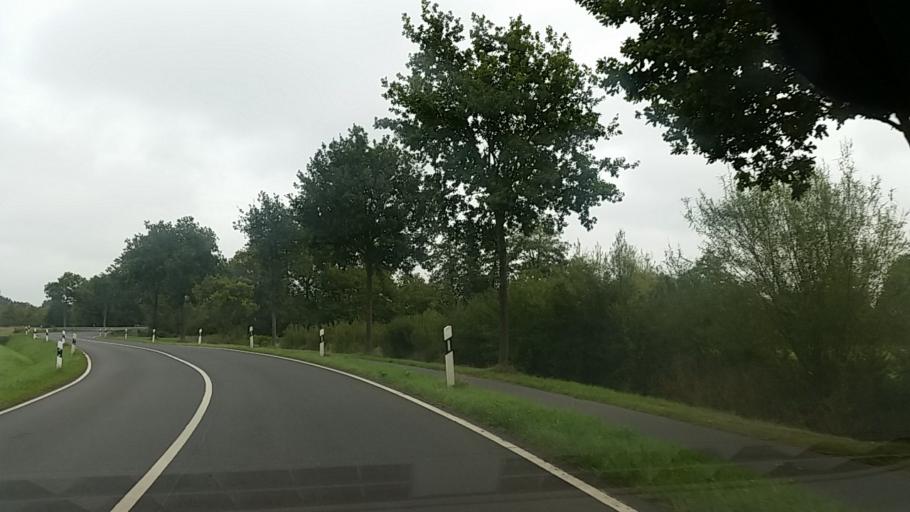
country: DE
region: Schleswig-Holstein
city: Kaltenkirchen
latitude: 53.8497
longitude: 9.9648
